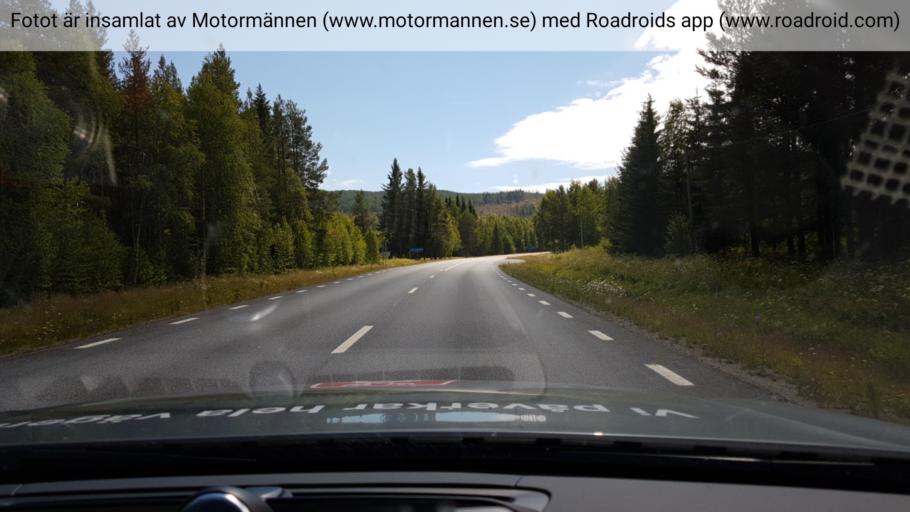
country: SE
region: Vaesterbotten
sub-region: Dorotea Kommun
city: Dorotea
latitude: 64.1876
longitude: 16.3042
